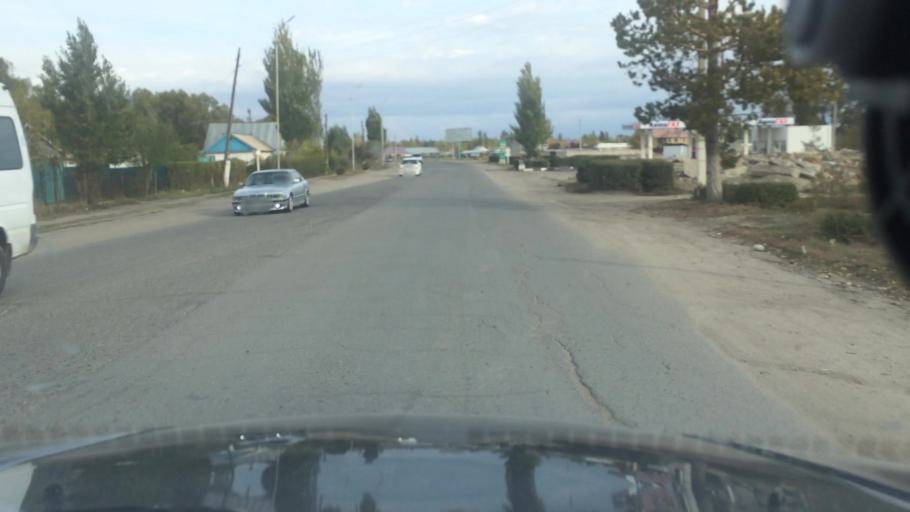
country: KG
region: Ysyk-Koel
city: Karakol
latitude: 42.5213
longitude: 78.3860
